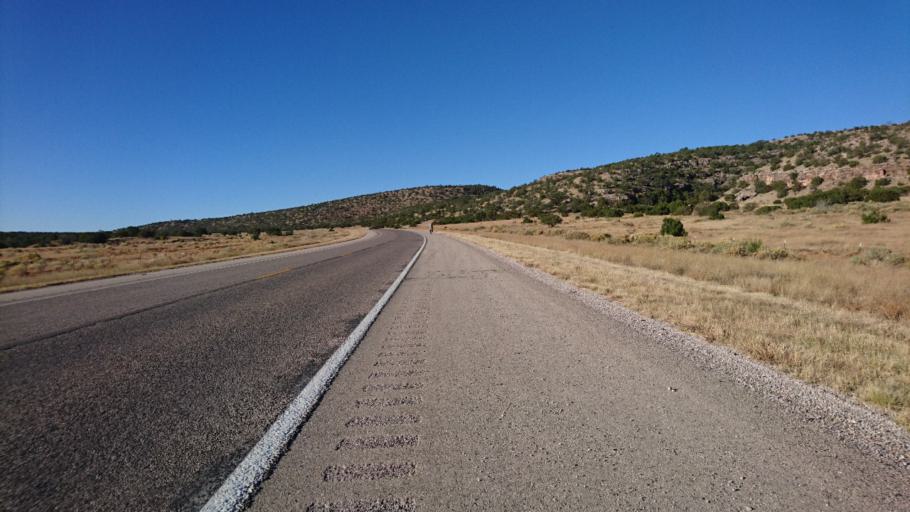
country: US
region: New Mexico
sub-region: Cibola County
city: Grants
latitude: 34.9780
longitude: -107.9090
